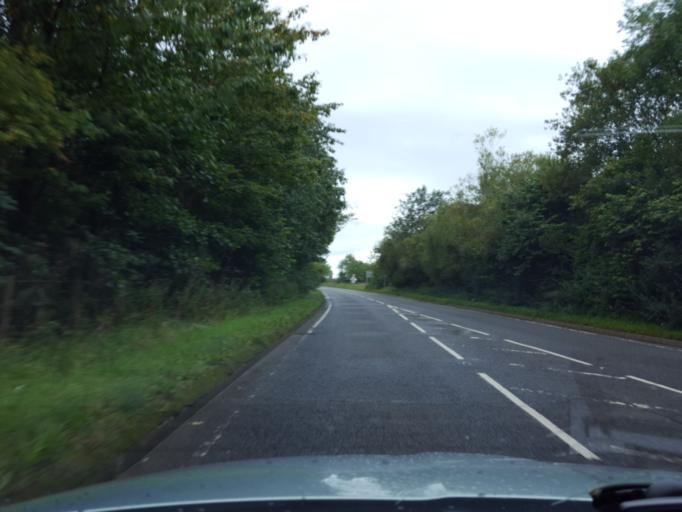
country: GB
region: Scotland
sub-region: Midlothian
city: Loanhead
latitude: 55.8577
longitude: -3.1353
